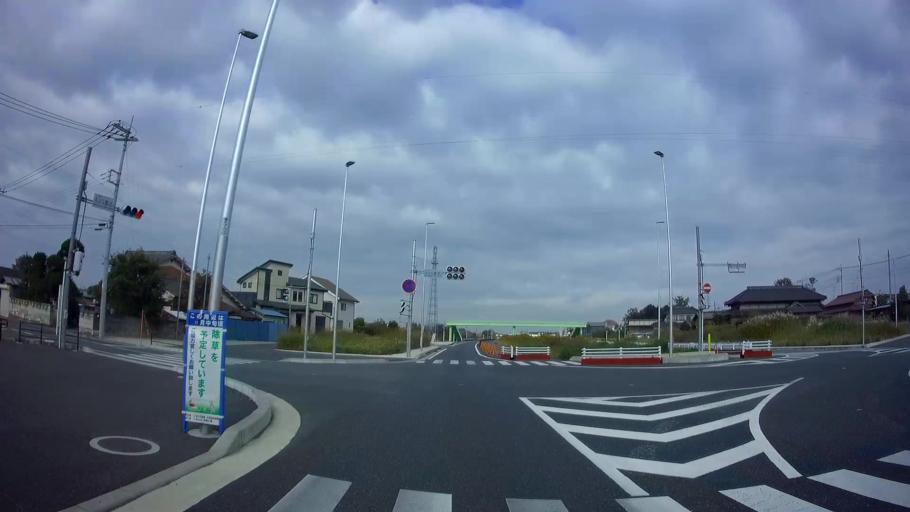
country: JP
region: Saitama
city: Okegawa
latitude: 35.9656
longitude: 139.5509
